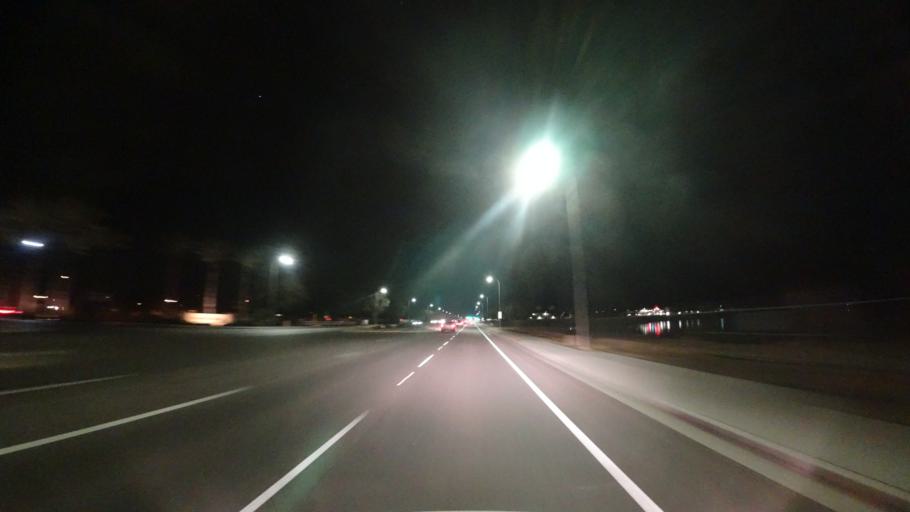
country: US
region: Arizona
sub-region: Maricopa County
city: Chandler
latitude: 33.2395
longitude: -111.7896
